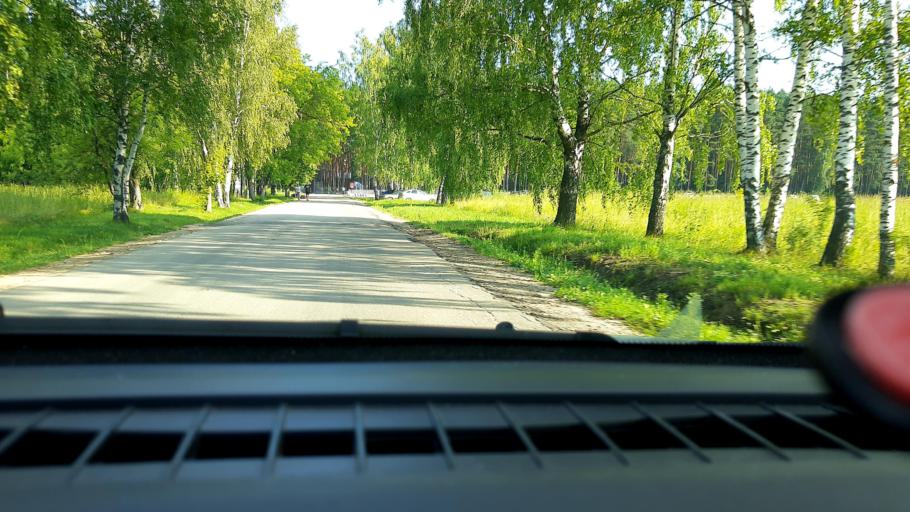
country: RU
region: Nizjnij Novgorod
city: Babino
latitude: 56.1423
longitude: 43.6509
